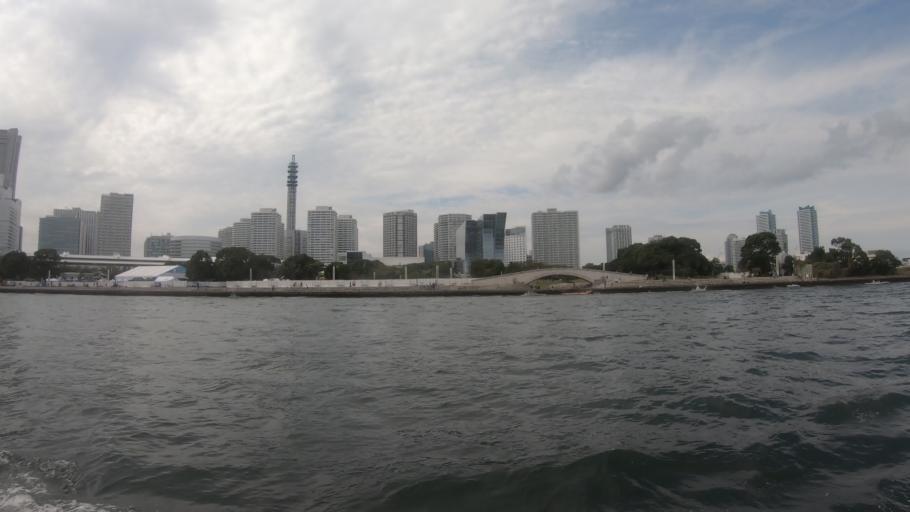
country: JP
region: Kanagawa
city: Yokohama
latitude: 35.4617
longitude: 139.6394
